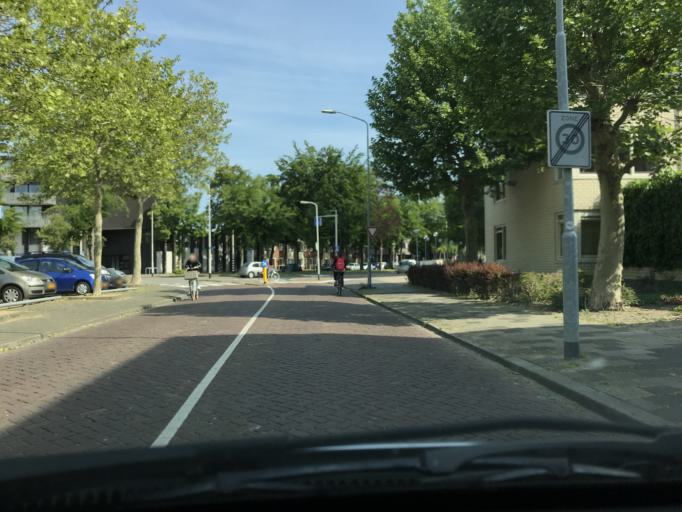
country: NL
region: North Brabant
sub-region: Gemeente Breda
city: Hoge Vucht
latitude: 51.5907
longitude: 4.8025
